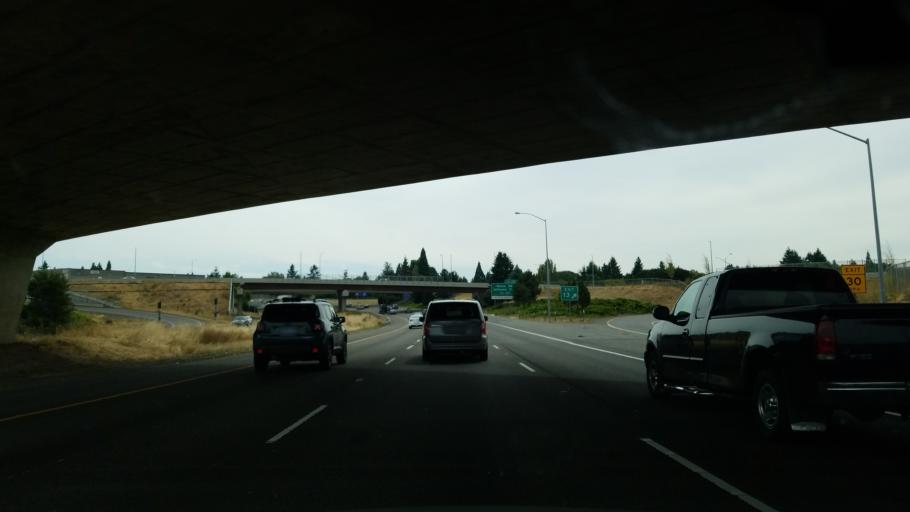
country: US
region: Oregon
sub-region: Clackamas County
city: Clackamas
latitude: 45.4206
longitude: -122.5728
